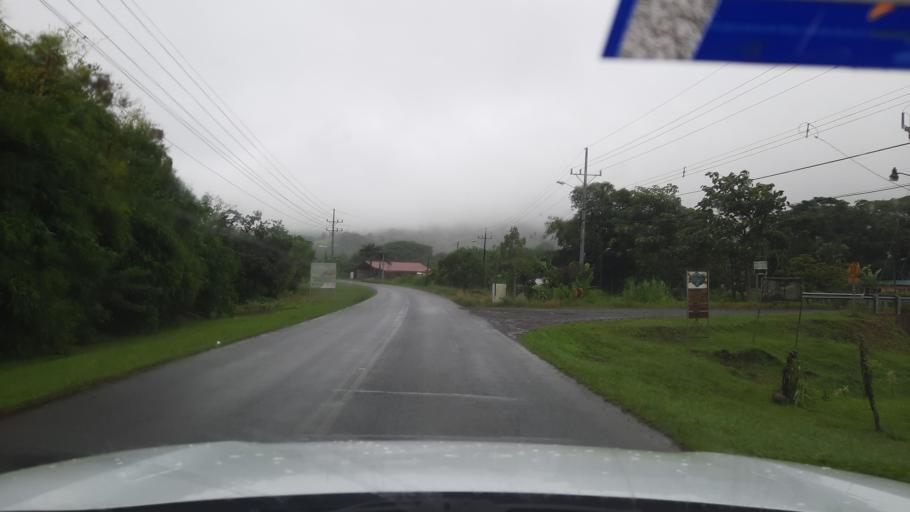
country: CR
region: Alajuela
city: Bijagua
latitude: 10.7241
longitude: -85.0665
